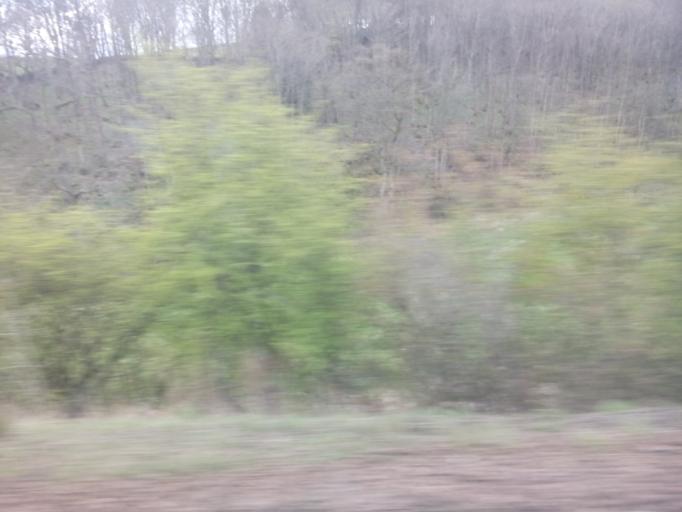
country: GB
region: Scotland
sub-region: The Scottish Borders
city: Chirnside
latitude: 55.8798
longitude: -2.2871
